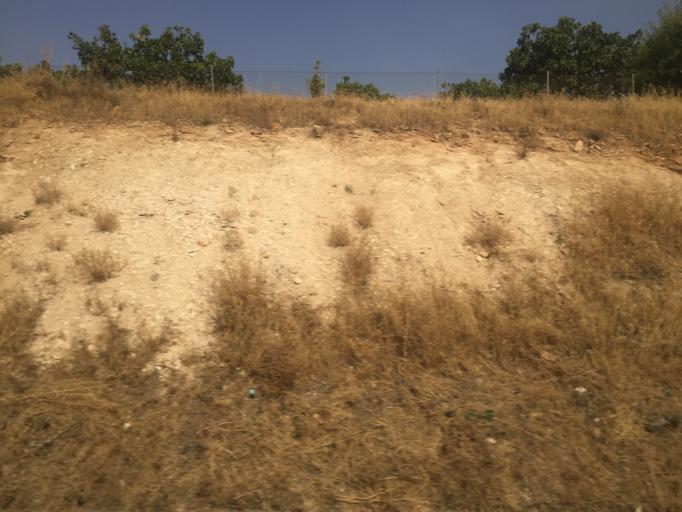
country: TR
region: Sanliurfa
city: Akziyaret
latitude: 37.2699
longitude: 38.8015
